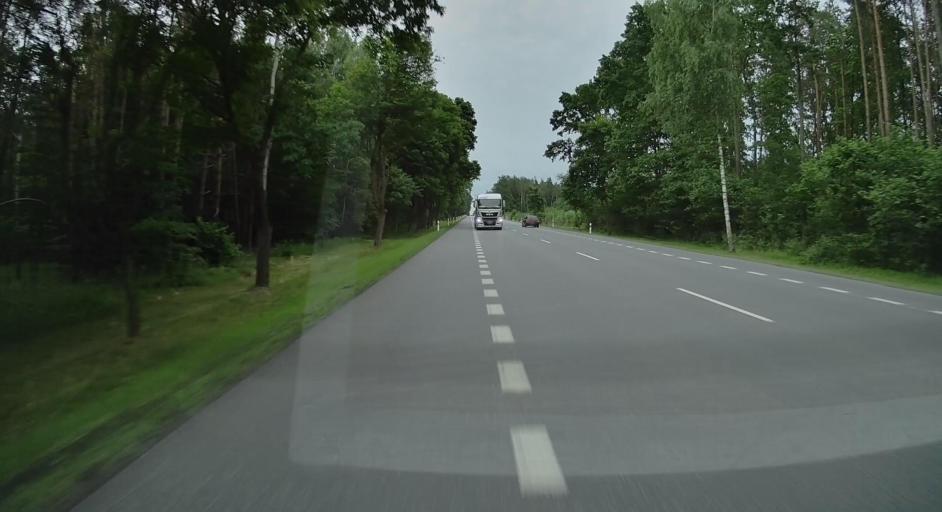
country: PL
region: Lublin Voivodeship
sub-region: Powiat bialski
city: Zalesie
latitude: 52.0361
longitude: 23.4110
